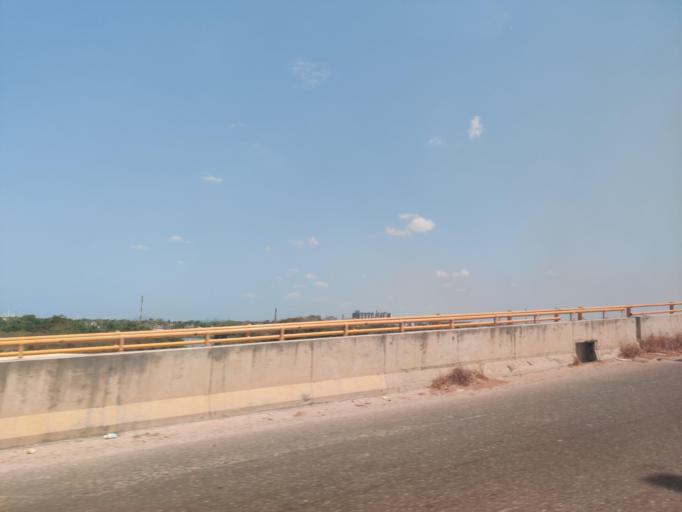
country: CO
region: Bolivar
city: Turbana
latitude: 10.2763
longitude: -75.5200
